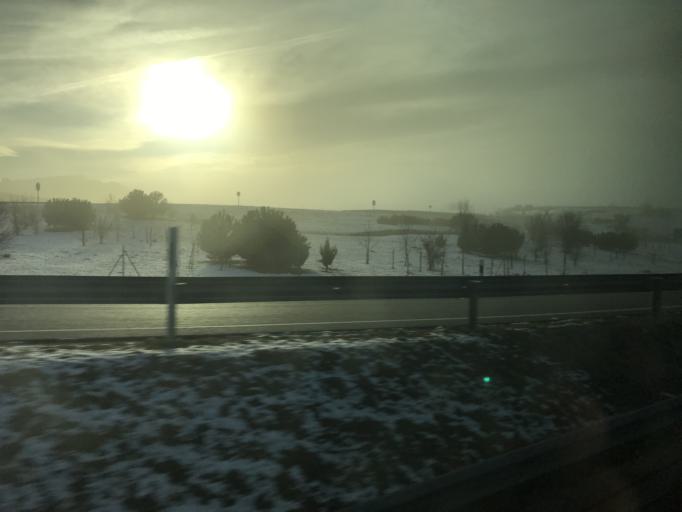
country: ES
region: Basque Country
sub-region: Provincia de Alava
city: Arminon
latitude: 42.7293
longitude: -2.8725
